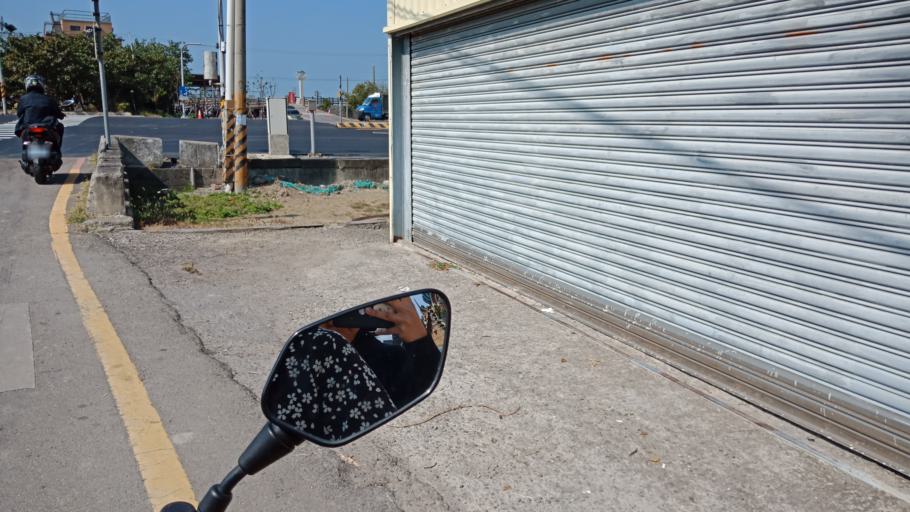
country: TW
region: Taiwan
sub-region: Hsinchu
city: Hsinchu
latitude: 24.7834
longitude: 120.9161
